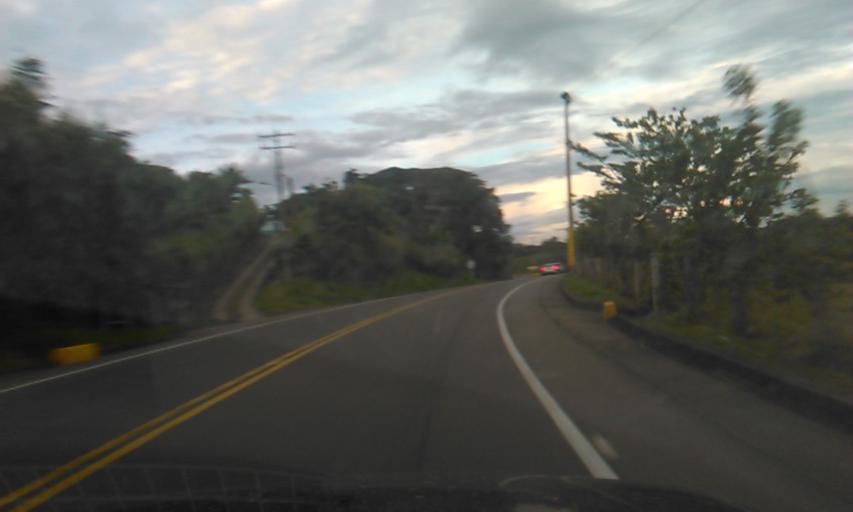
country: CO
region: Quindio
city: La Tebaida
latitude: 4.4290
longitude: -75.8609
